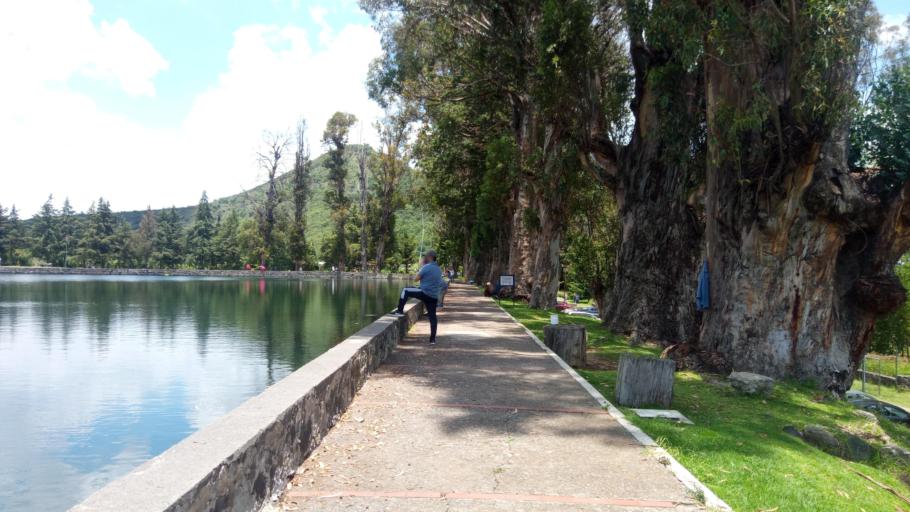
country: MX
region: Puebla
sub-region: Tianguismanalco
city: San Martin Tlapala
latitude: 18.9447
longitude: -98.4704
